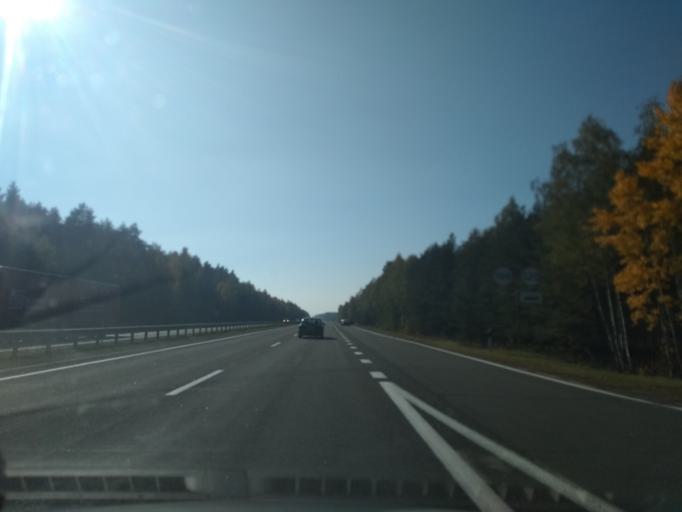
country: BY
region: Brest
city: Ivatsevichy
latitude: 52.8201
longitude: 25.5865
